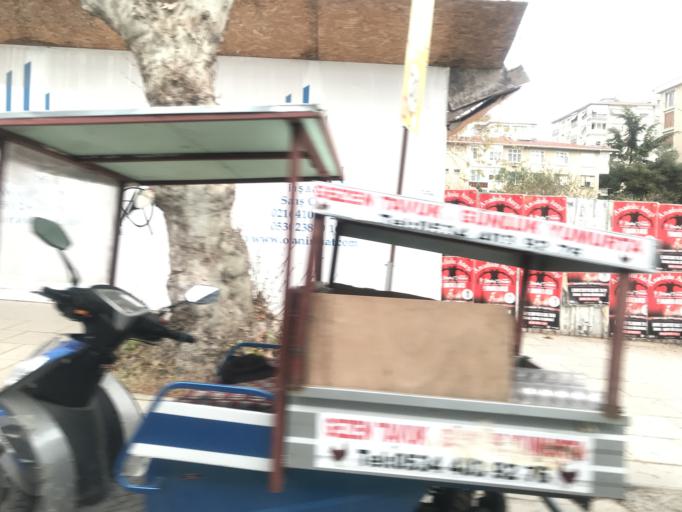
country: TR
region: Istanbul
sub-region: Atasehir
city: Atasehir
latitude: 40.9625
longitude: 29.0911
